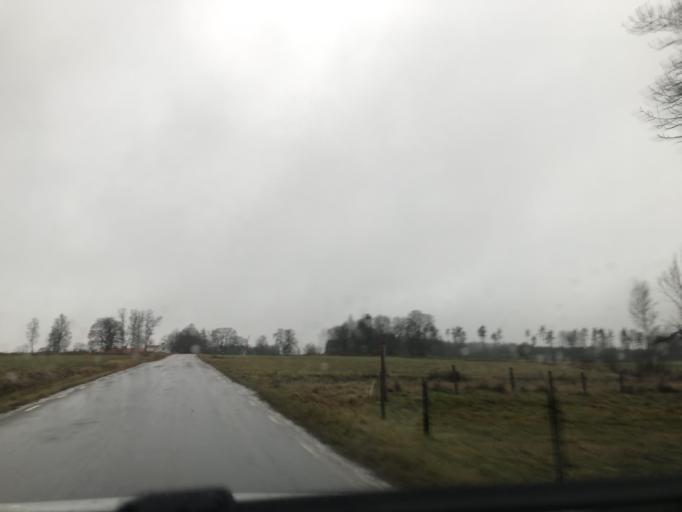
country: SE
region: Vaestra Goetaland
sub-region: Ulricehamns Kommun
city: Ulricehamn
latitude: 57.8480
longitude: 13.5421
